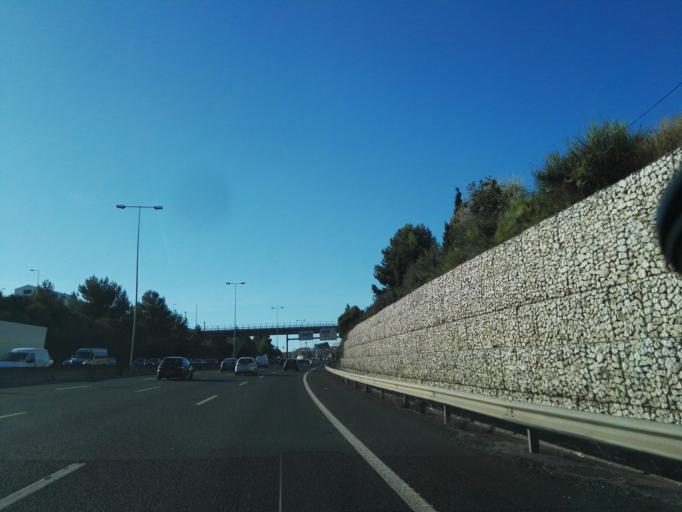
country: PT
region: Lisbon
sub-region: Loures
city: Camarate
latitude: 38.7970
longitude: -9.1224
